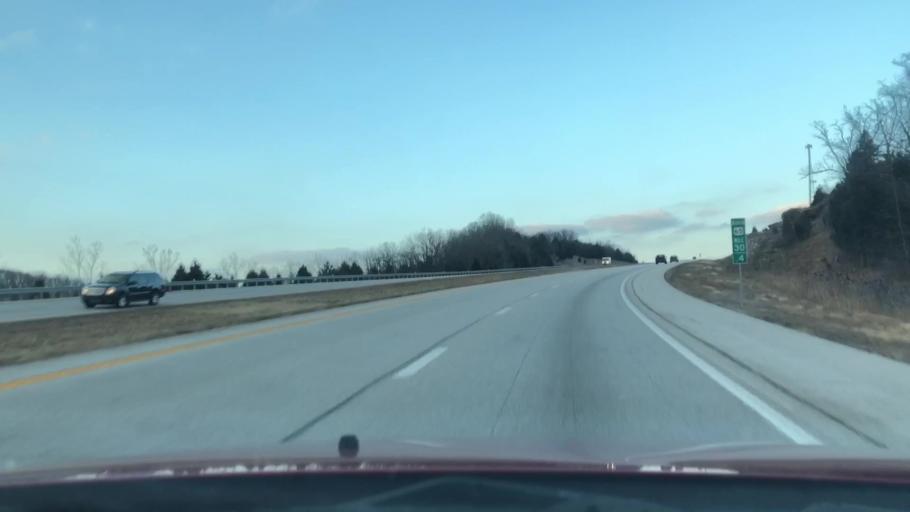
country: US
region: Missouri
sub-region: Christian County
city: Ozark
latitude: 36.9126
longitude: -93.2446
